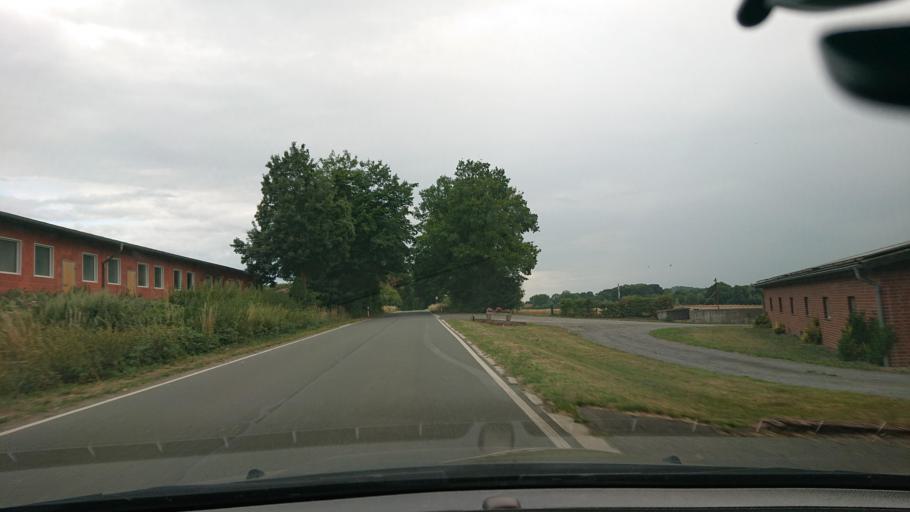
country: DE
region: North Rhine-Westphalia
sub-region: Regierungsbezirk Arnsberg
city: Hamm
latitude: 51.7160
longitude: 7.8487
